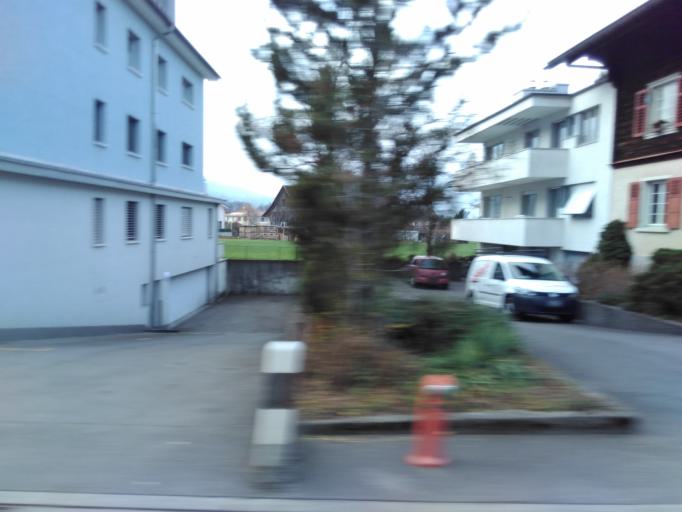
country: CH
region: Schwyz
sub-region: Bezirk March
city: Schubelbach
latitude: 47.1780
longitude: 8.8979
